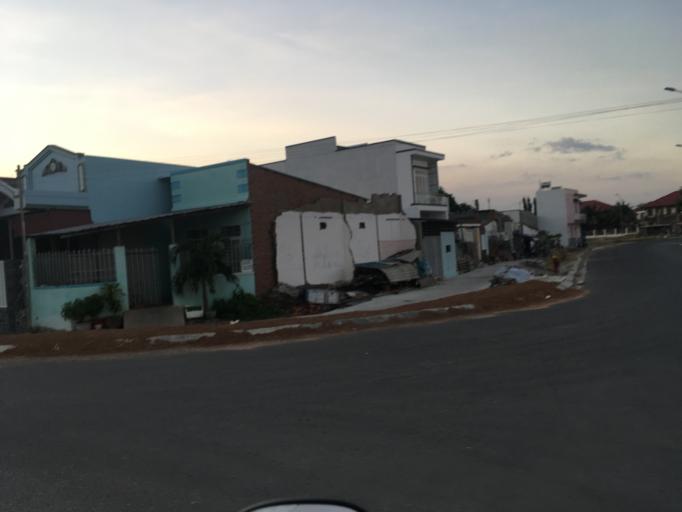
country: VN
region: Ninh Thuan
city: Phan Rang-Thap Cham
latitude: 11.5728
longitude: 108.9964
